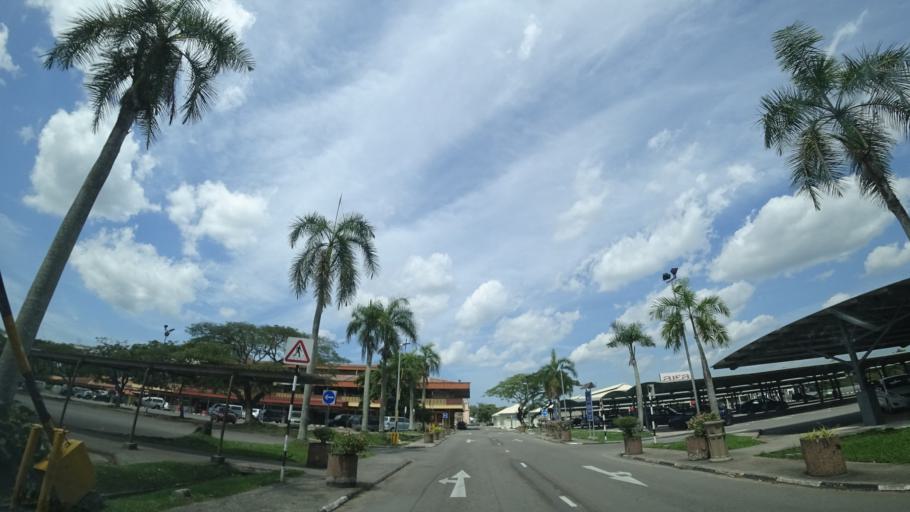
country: BN
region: Brunei and Muara
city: Bandar Seri Begawan
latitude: 4.9031
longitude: 114.9187
